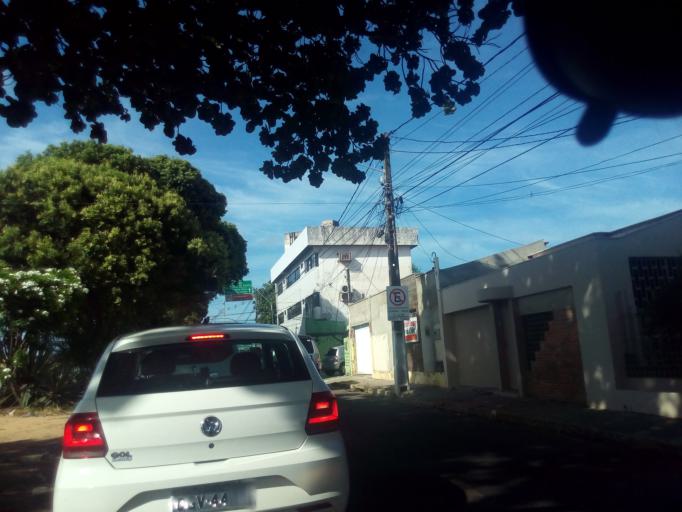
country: BR
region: Rio Grande do Norte
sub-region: Natal
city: Natal
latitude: -5.8161
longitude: -35.2138
